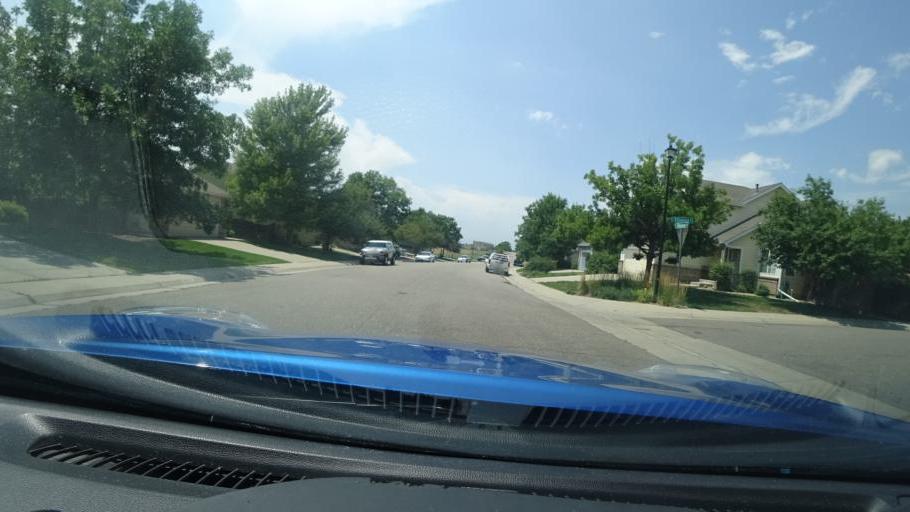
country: US
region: Colorado
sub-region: Adams County
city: Aurora
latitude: 39.6682
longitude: -104.7576
